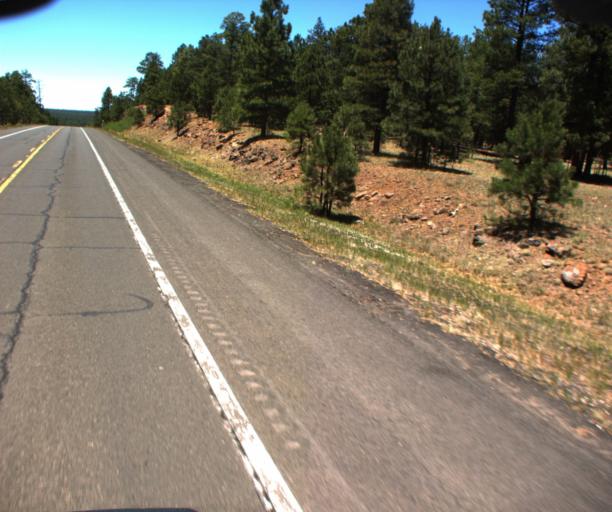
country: US
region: Arizona
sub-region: Gila County
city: Pine
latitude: 34.5526
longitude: -111.2952
